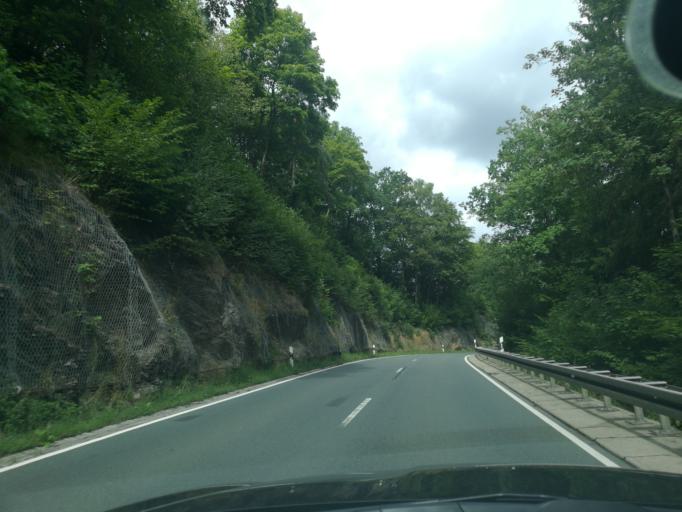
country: DE
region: Saxony
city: Adorf
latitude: 50.3478
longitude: 12.2353
